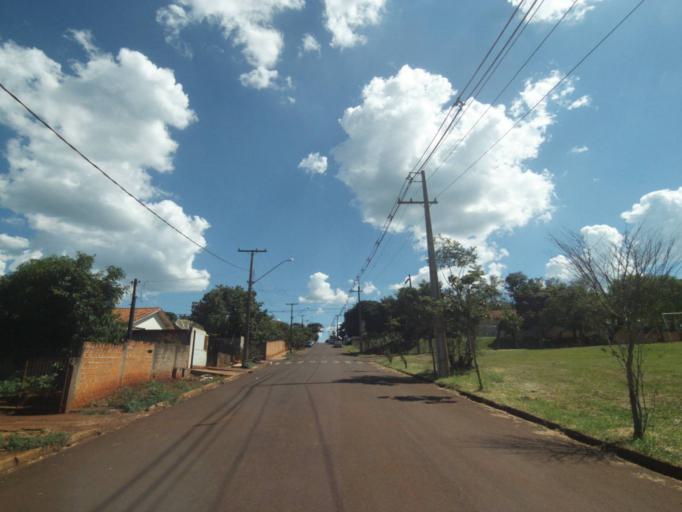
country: BR
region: Parana
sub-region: Sertanopolis
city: Sertanopolis
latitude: -23.0403
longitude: -50.8217
